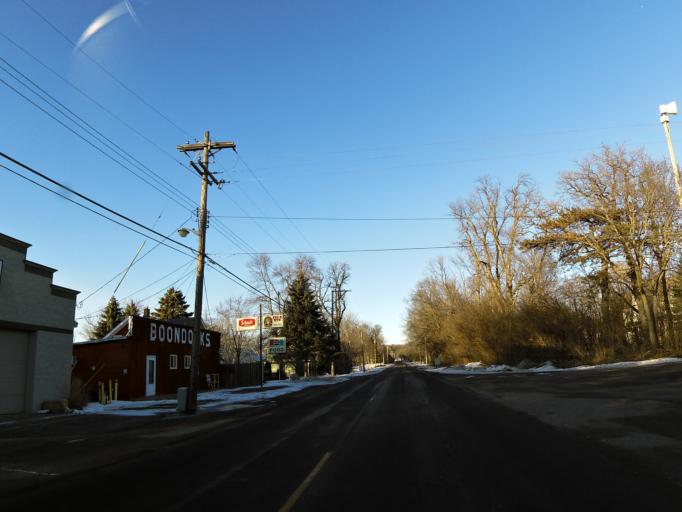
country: US
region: Minnesota
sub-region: Washington County
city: Cottage Grove
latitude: 44.8413
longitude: -92.8819
